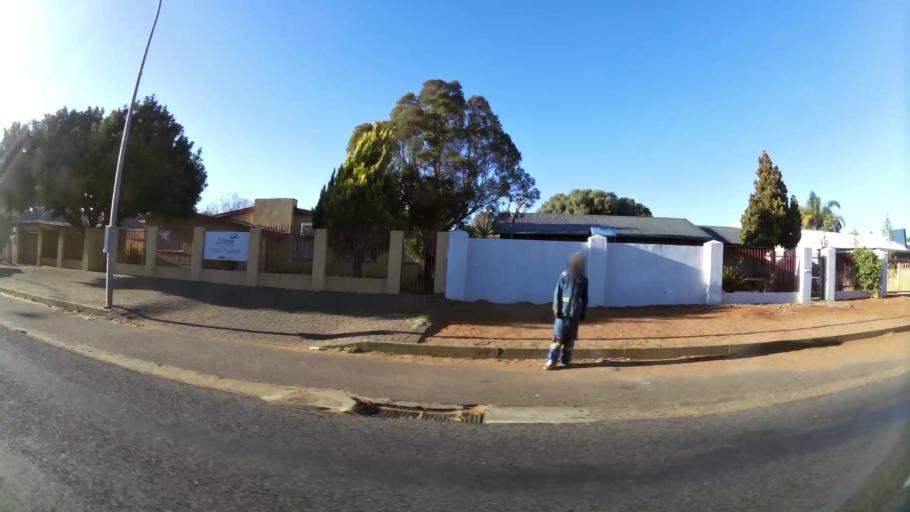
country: ZA
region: Northern Cape
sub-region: Frances Baard District Municipality
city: Kimberley
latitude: -28.7469
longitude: 24.7441
